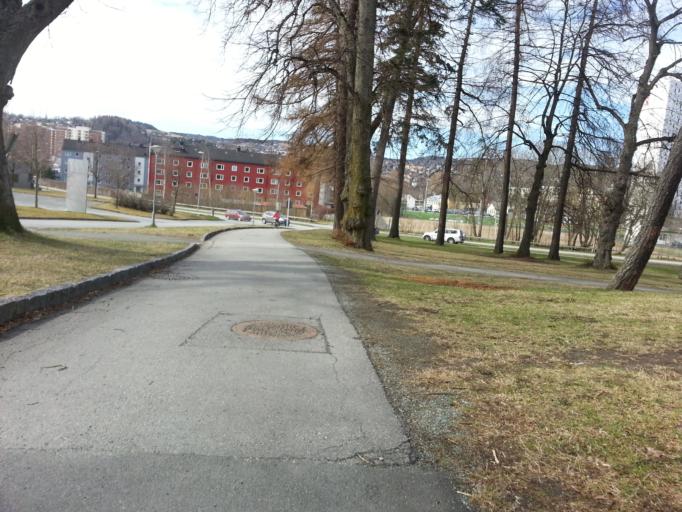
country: NO
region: Sor-Trondelag
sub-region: Trondheim
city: Trondheim
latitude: 63.4096
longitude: 10.4077
